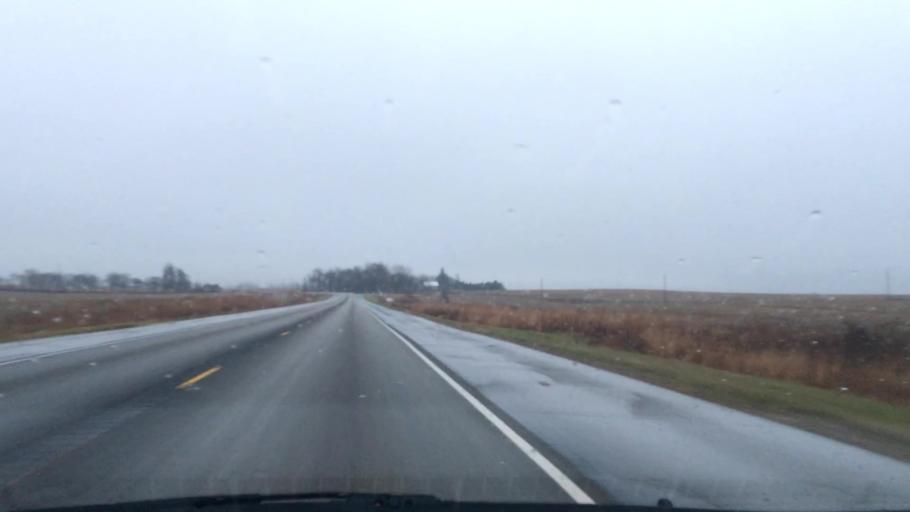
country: US
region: Minnesota
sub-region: Fillmore County
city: Harmony
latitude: 43.5177
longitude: -91.8990
